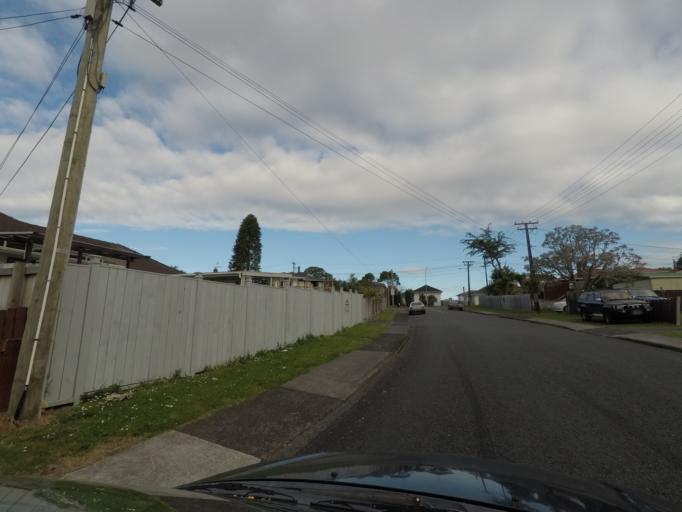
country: NZ
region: Auckland
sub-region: Auckland
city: Rosebank
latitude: -36.8855
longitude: 174.6550
